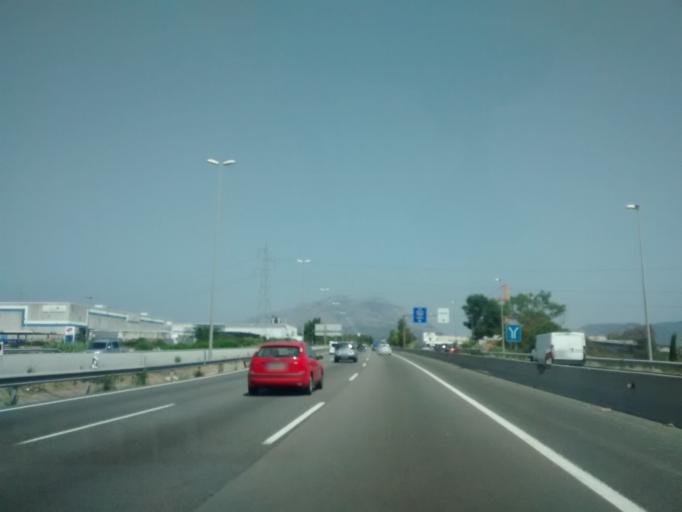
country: ES
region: Catalonia
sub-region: Provincia de Barcelona
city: Abrera
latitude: 41.5071
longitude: 1.9046
